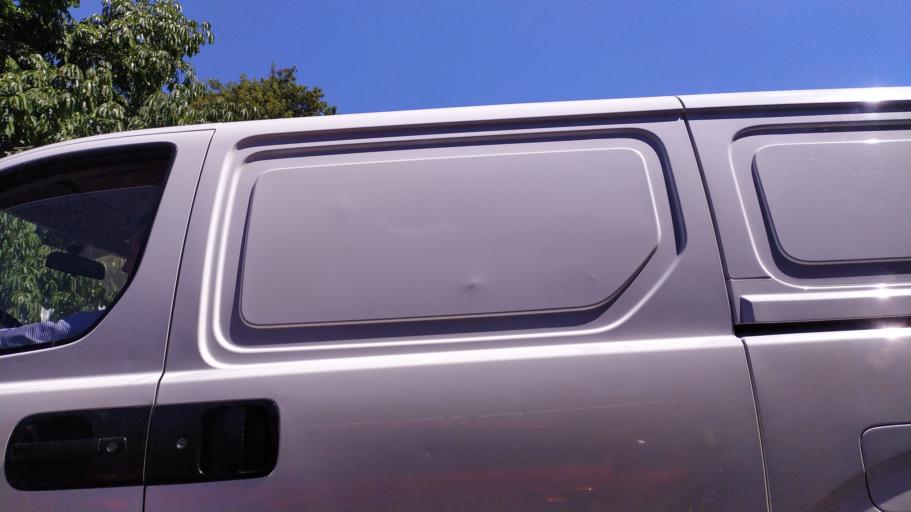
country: MX
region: Jalisco
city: Zapopan2
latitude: 20.6898
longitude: -103.4122
